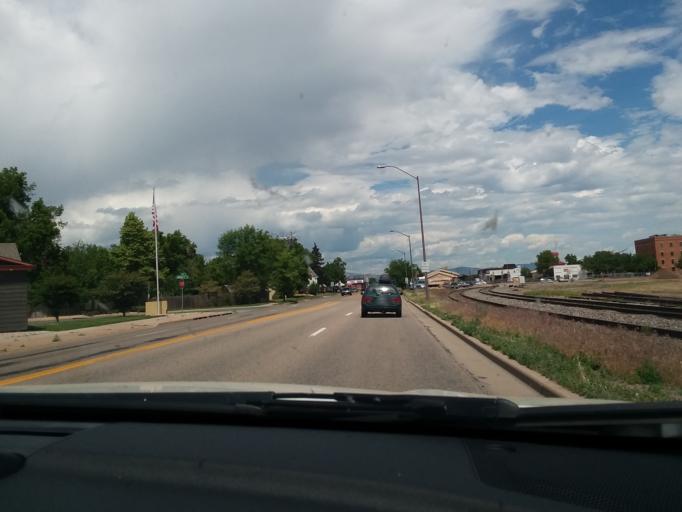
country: US
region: Colorado
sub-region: Larimer County
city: Fort Collins
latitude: 40.5858
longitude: -105.0695
